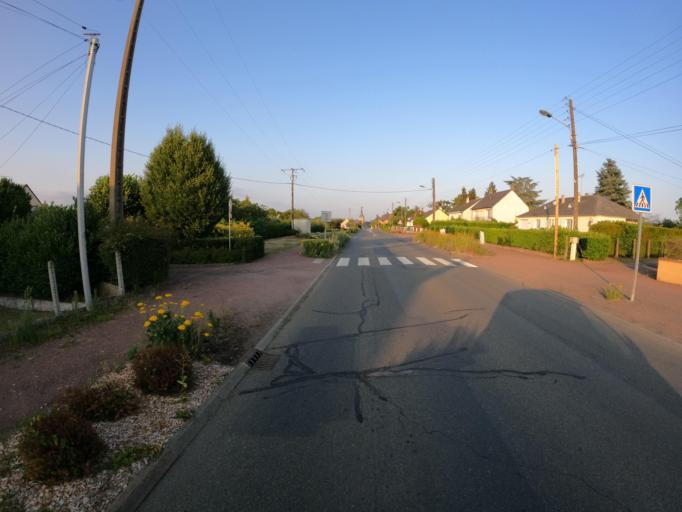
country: FR
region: Pays de la Loire
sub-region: Departement de la Sarthe
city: Parce-sur-Sarthe
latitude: 47.8434
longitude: -0.2050
